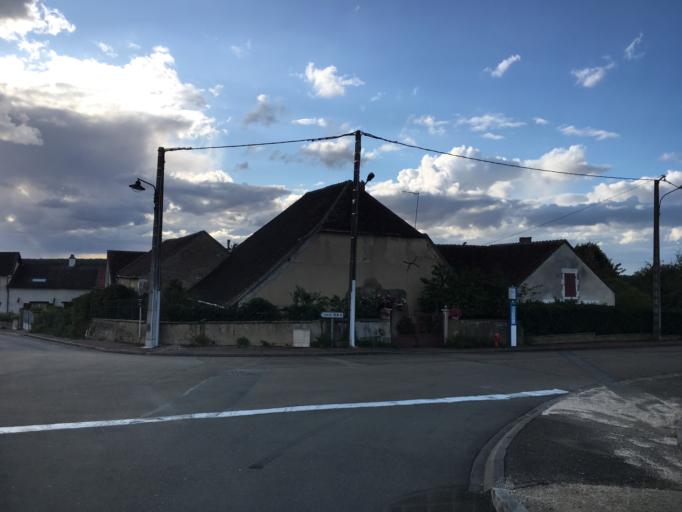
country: FR
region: Bourgogne
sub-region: Departement de l'Yonne
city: Saint-Georges-sur-Baulche
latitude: 47.8253
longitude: 3.5444
